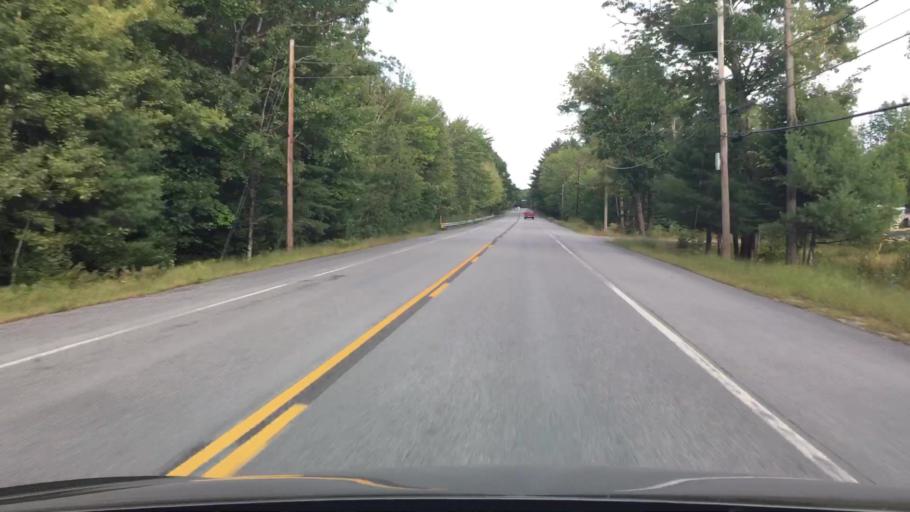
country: US
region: Maine
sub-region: Cumberland County
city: Bridgton
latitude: 44.0657
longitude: -70.7489
